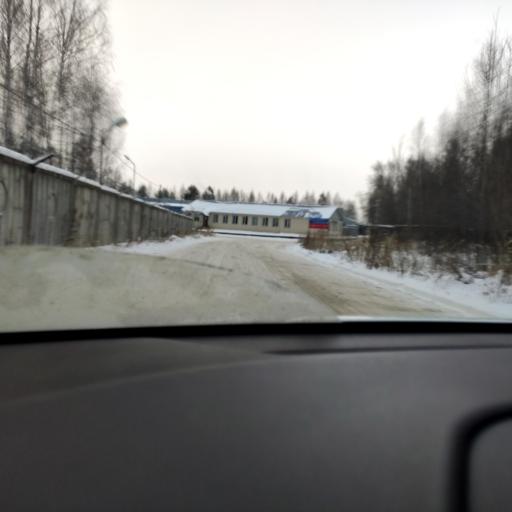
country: RU
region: Tatarstan
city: Osinovo
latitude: 55.8895
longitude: 48.8282
